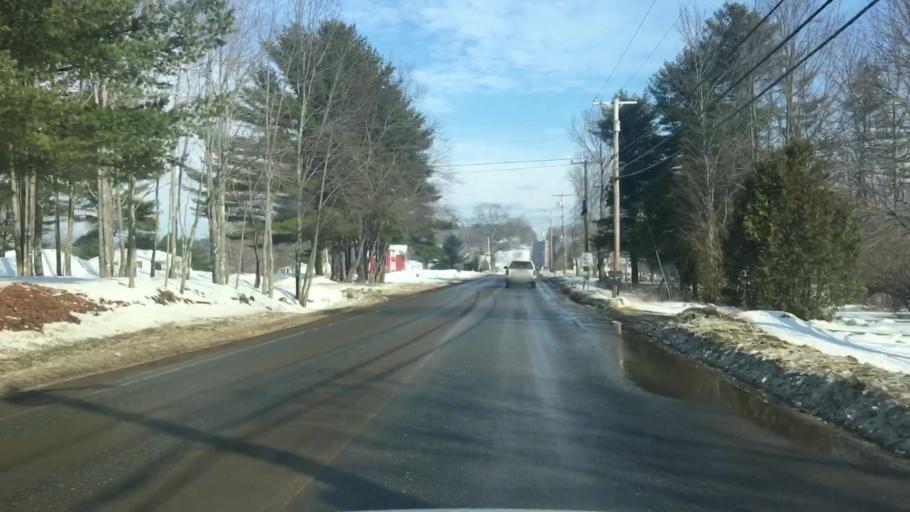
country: US
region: Maine
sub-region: Penobscot County
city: Hermon
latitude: 44.8275
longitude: -68.8872
